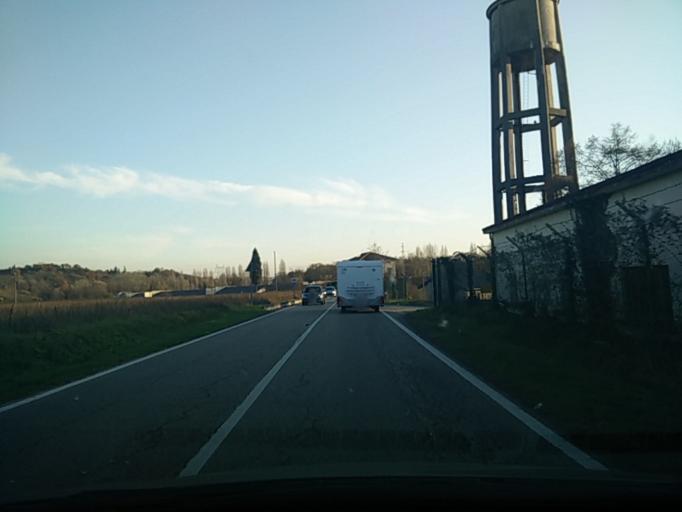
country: IT
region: Veneto
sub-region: Provincia di Verona
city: Salionze
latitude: 45.4225
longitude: 10.7070
